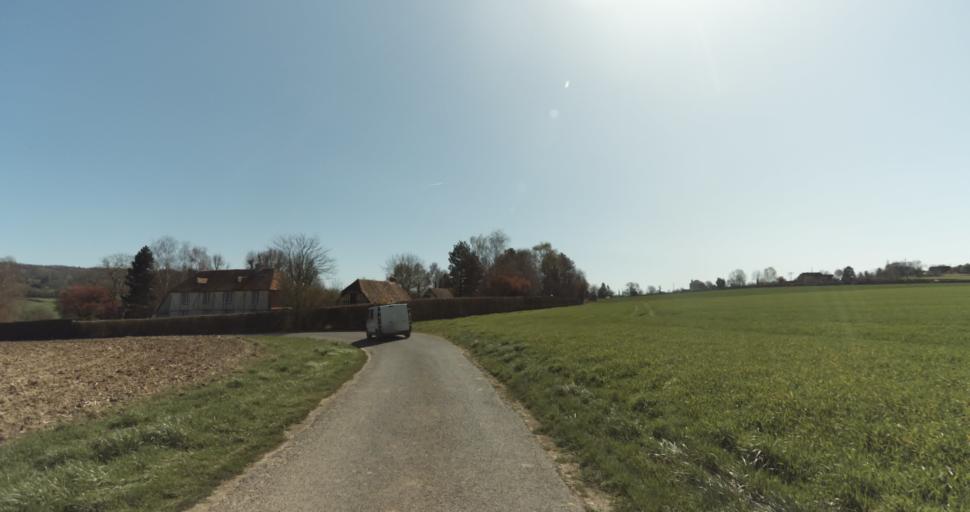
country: FR
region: Lower Normandy
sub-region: Departement du Calvados
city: Saint-Pierre-sur-Dives
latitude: 48.9937
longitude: 0.0259
